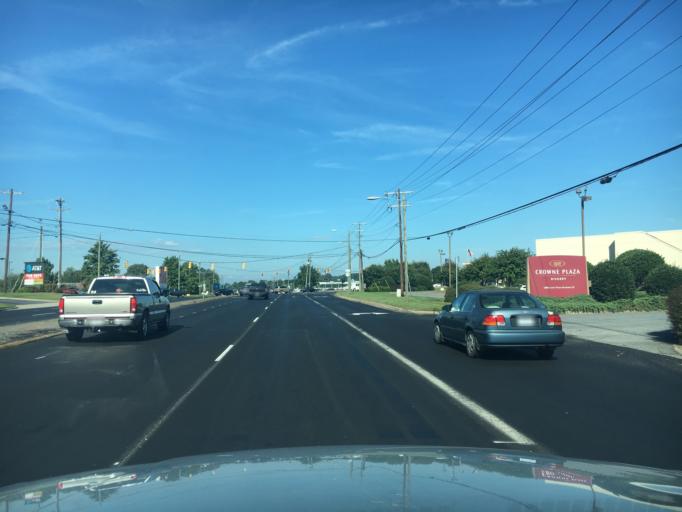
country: US
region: North Carolina
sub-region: Catawba County
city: Hickory
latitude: 35.7086
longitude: -81.3099
